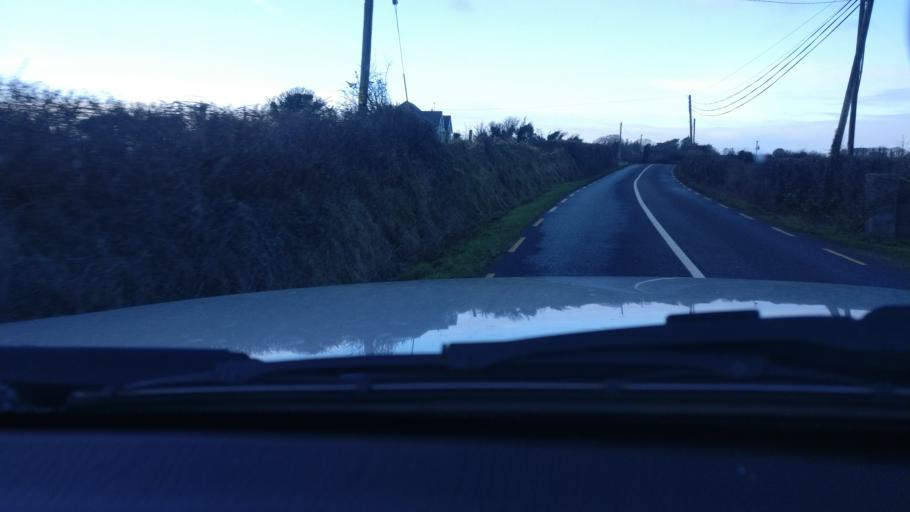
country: IE
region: Connaught
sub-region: County Galway
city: Loughrea
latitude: 53.2245
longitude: -8.4025
